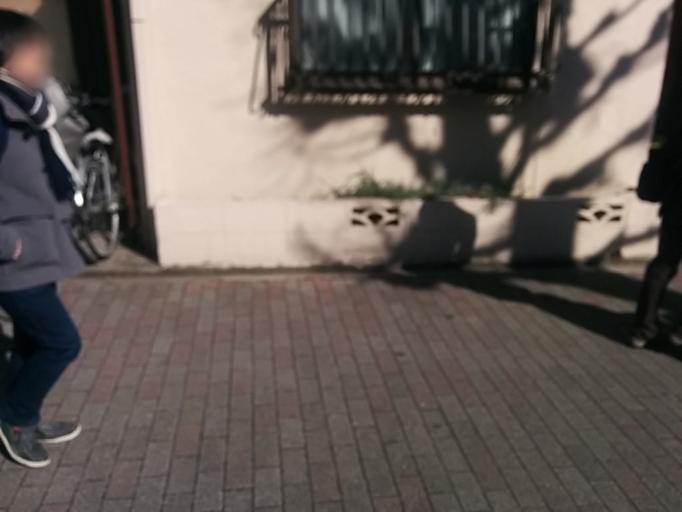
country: JP
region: Tokyo
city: Tokyo
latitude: 35.7319
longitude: 139.7500
